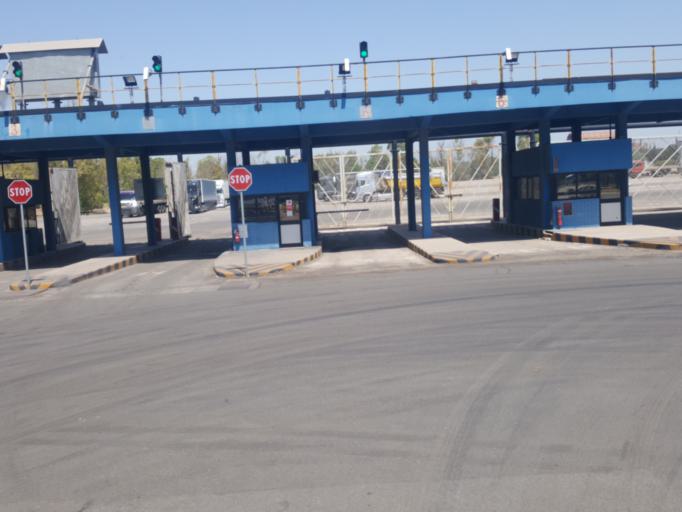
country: IT
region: Apulia
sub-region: Provincia di Taranto
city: Statte
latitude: 40.5159
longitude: 17.1878
